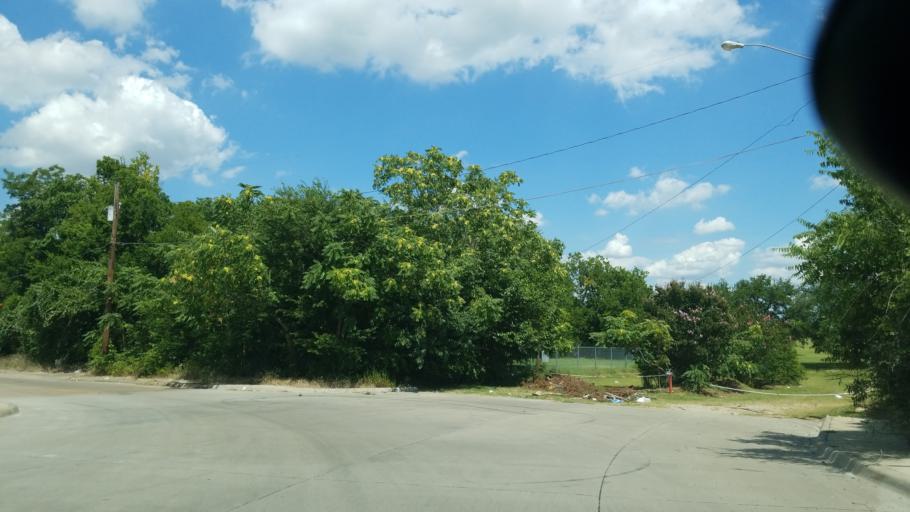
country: US
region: Texas
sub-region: Dallas County
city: Dallas
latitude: 32.7464
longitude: -96.7510
